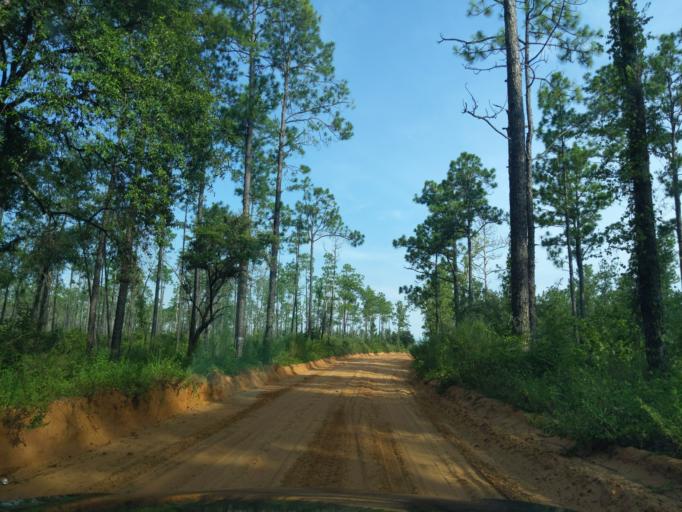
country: US
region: Florida
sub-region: Gadsden County
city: Midway
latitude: 30.4006
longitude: -84.4117
